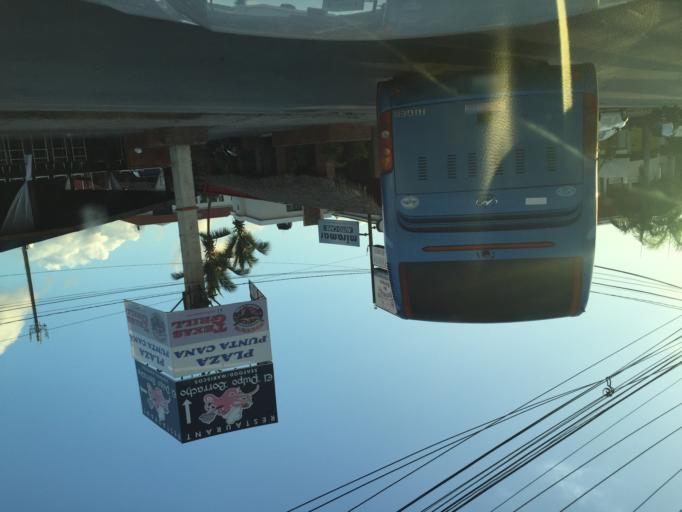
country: DO
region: San Juan
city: Punta Cana
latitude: 18.6911
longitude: -68.4381
